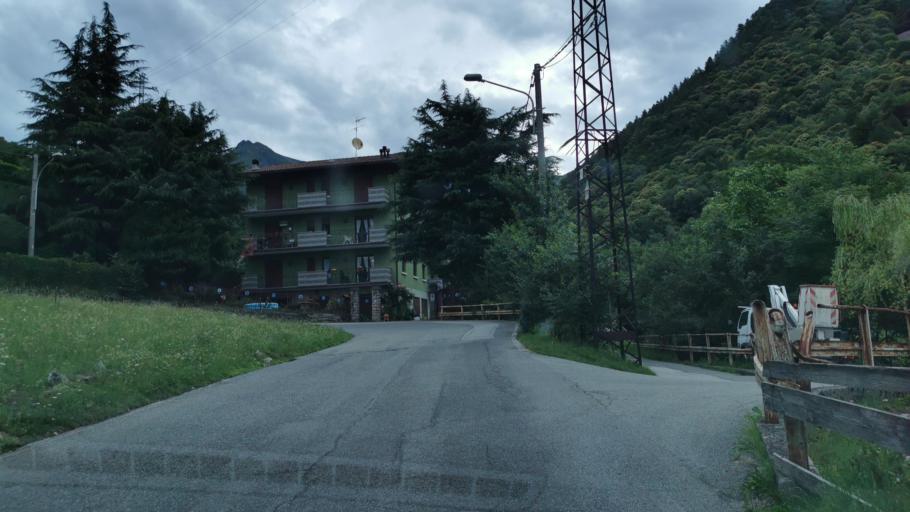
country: IT
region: Lombardy
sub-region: Provincia di Lecco
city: Casargo
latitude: 46.0437
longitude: 9.3914
